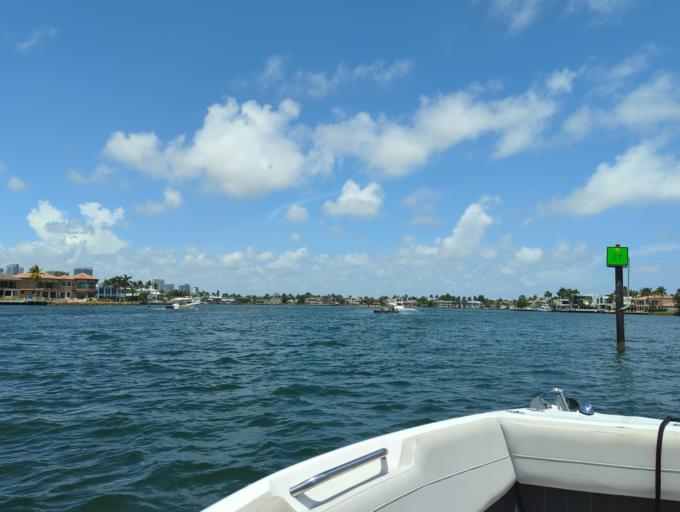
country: US
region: Florida
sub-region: Broward County
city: Fort Lauderdale
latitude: 26.1033
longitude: -80.1192
